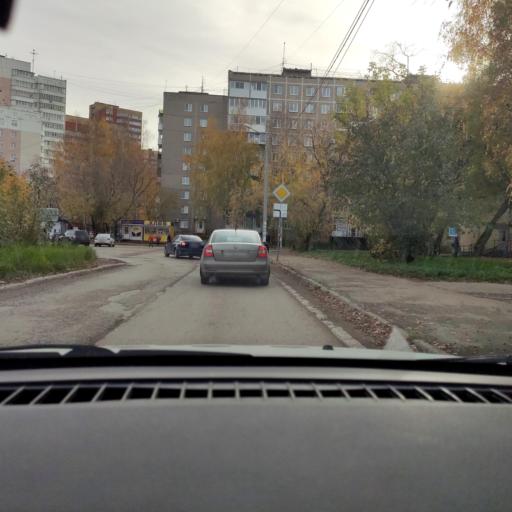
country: RU
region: Perm
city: Perm
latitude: 58.0633
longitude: 56.3520
